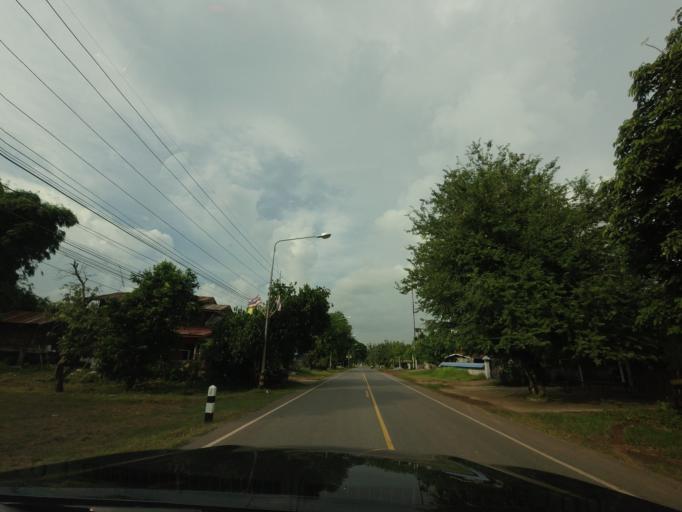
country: TH
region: Changwat Nong Bua Lamphu
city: Suwannakhuha
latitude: 17.5526
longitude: 102.3902
